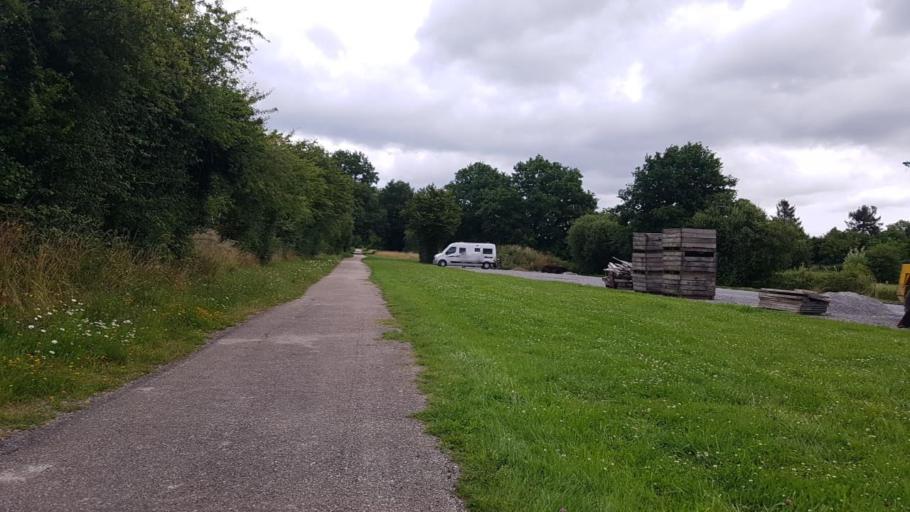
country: FR
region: Picardie
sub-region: Departement de l'Aisne
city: Buironfosse
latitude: 49.9065
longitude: 3.7838
